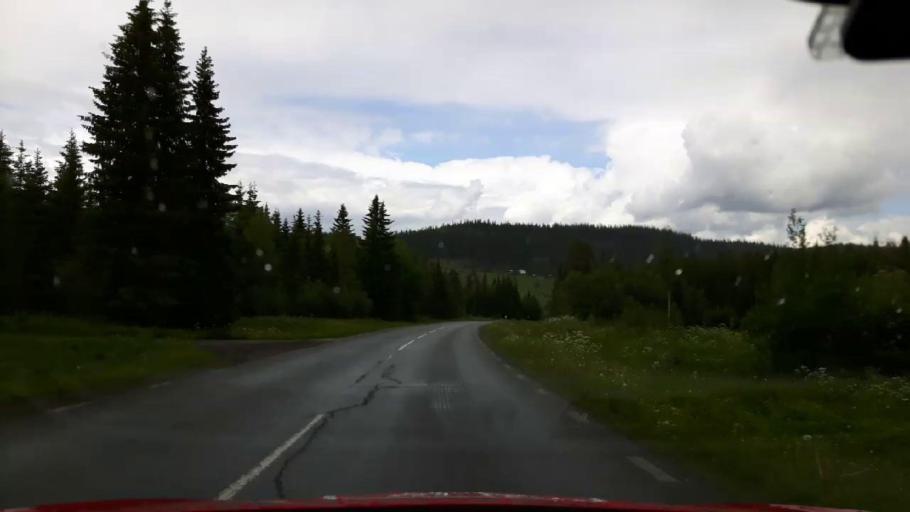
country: SE
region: Jaemtland
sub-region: Krokoms Kommun
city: Krokom
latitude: 63.4787
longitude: 14.1909
